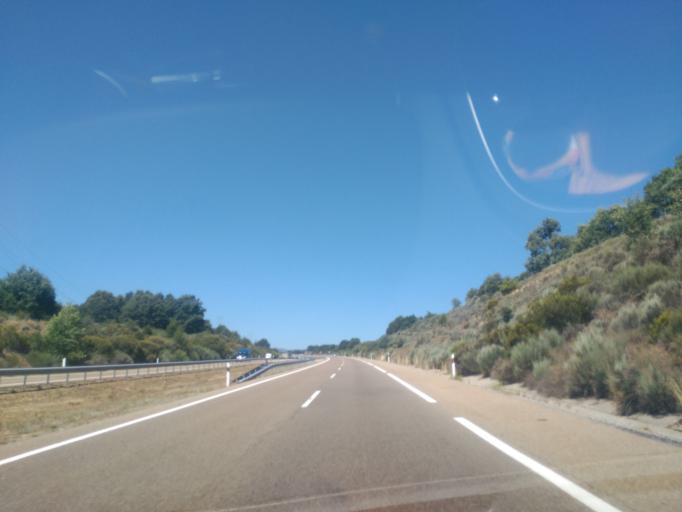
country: ES
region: Castille and Leon
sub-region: Provincia de Zamora
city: Palacios de Sanabria
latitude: 42.0469
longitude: -6.5152
